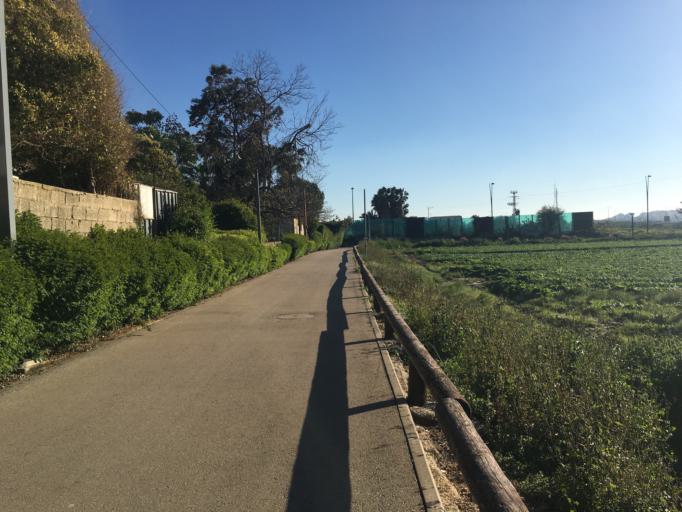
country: IL
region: Tel Aviv
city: Ramat HaSharon
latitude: 32.1412
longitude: 34.8235
